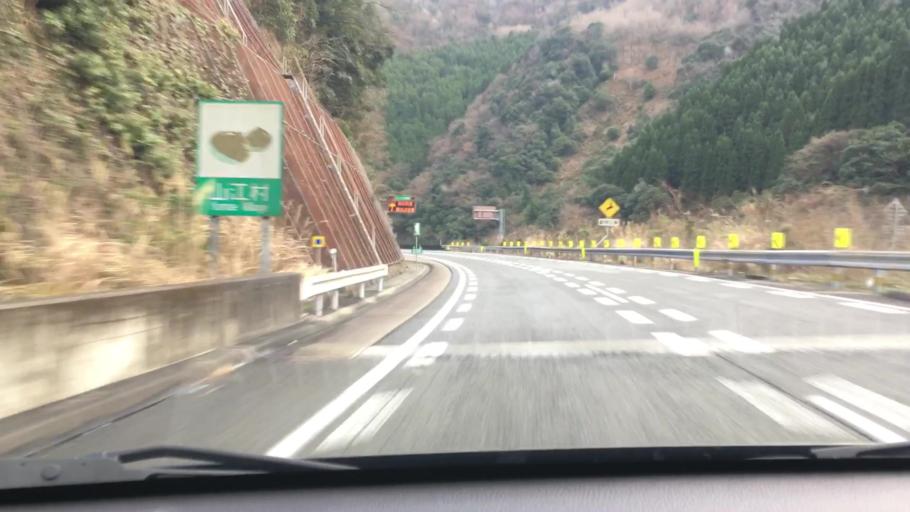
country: JP
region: Kumamoto
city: Hitoyoshi
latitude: 32.3328
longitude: 130.7395
